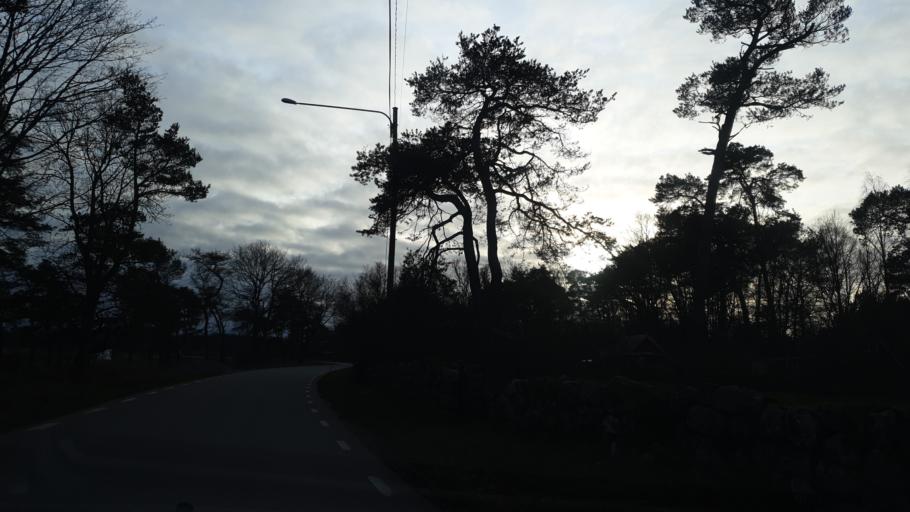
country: SE
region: Kalmar
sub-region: Torsas Kommun
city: Torsas
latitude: 56.2673
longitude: 16.0319
